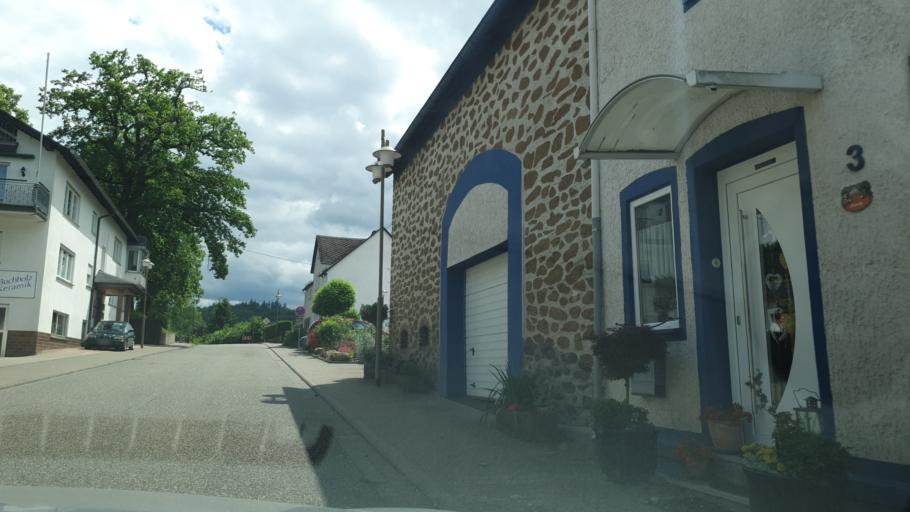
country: DE
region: Rheinland-Pfalz
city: Hillscheid
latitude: 50.3995
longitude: 7.6961
